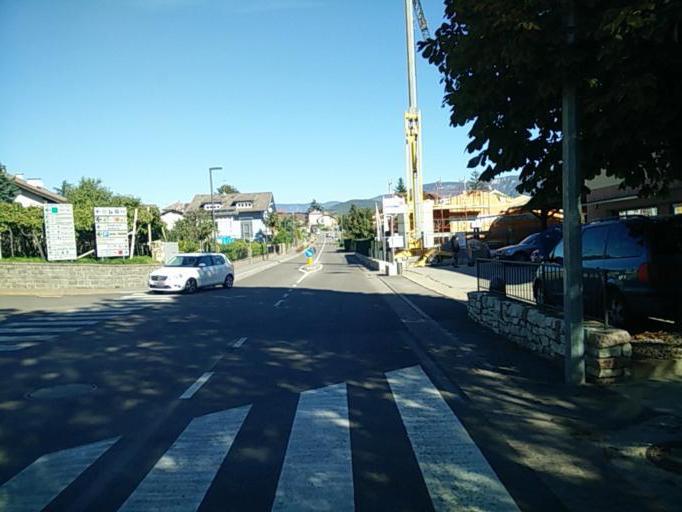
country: IT
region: Trentino-Alto Adige
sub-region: Bolzano
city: Termeno
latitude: 46.3396
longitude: 11.2422
